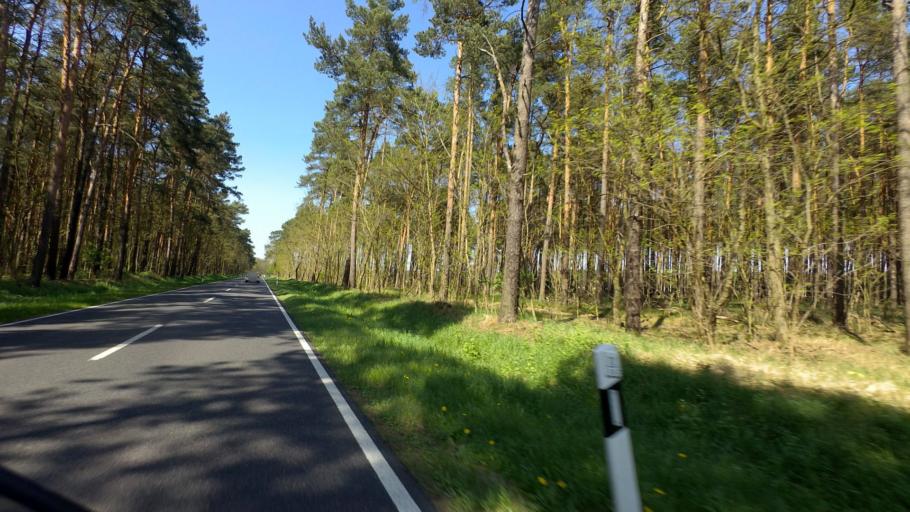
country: DE
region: Brandenburg
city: Friedland
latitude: 52.0475
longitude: 14.2872
